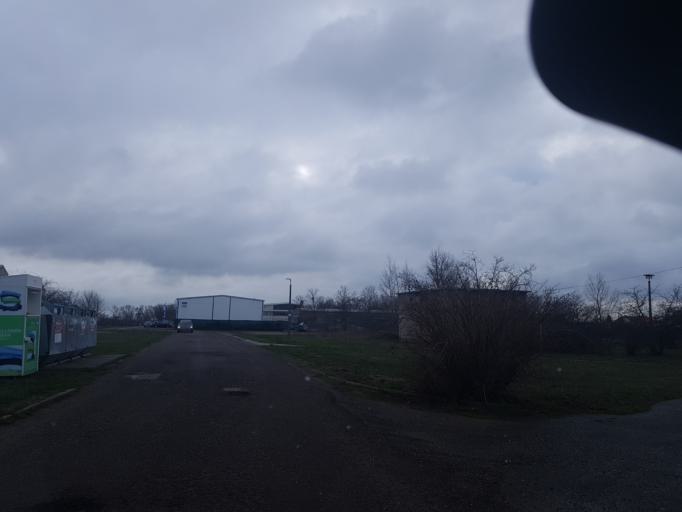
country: DE
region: Brandenburg
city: Muhlberg
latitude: 51.4323
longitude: 13.2283
